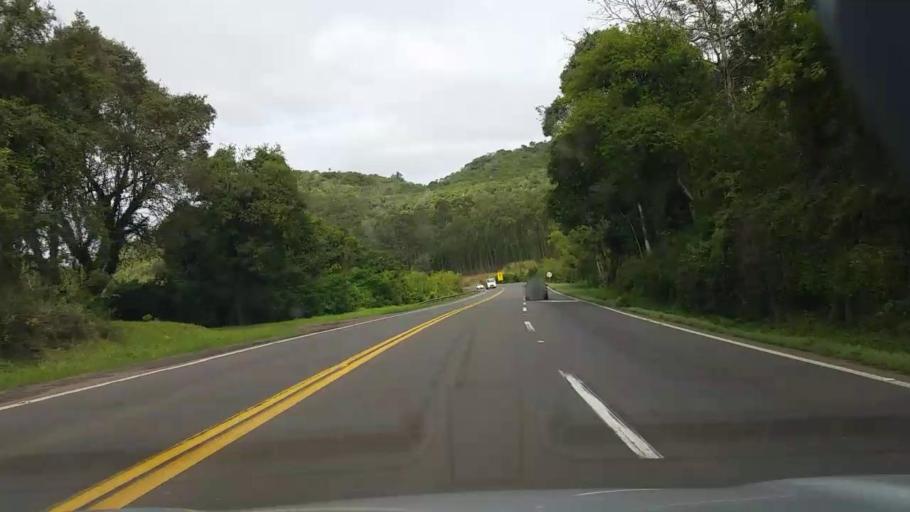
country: BR
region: Rio Grande do Sul
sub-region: Arroio Do Meio
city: Arroio do Meio
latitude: -29.3817
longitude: -52.0544
